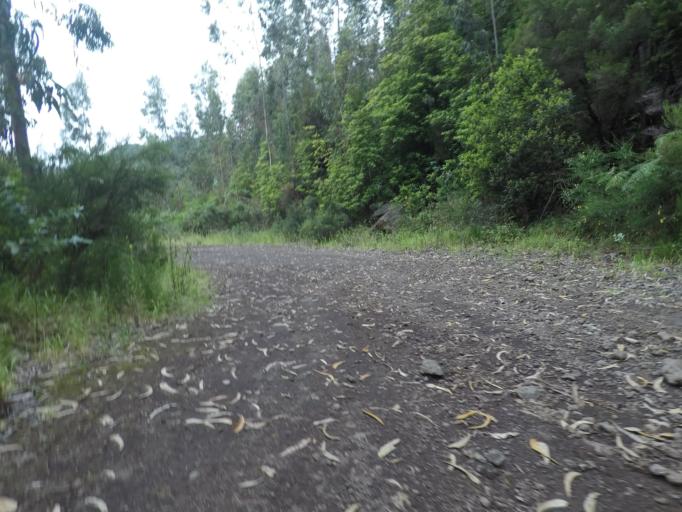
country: PT
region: Madeira
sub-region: Sao Vicente
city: Sao Vicente
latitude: 32.7741
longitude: -17.0506
